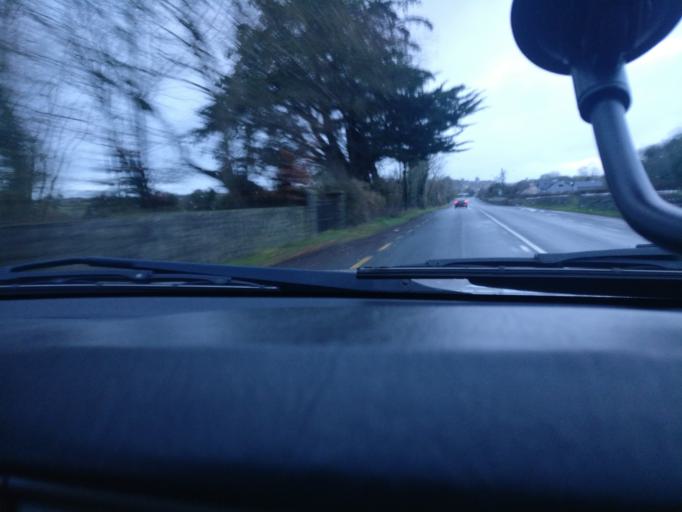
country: IE
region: Connaught
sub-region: County Galway
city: Ballinasloe
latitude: 53.3155
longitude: -8.2523
